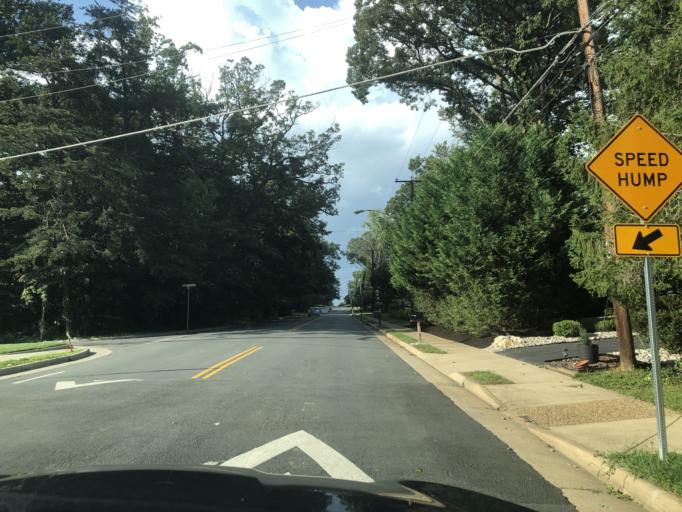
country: US
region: Virginia
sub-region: City of Fairfax
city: Fairfax
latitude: 38.8368
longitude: -77.2882
